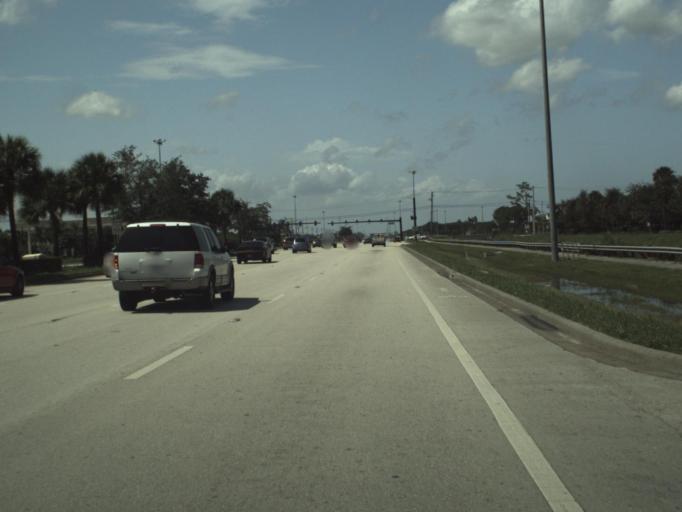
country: US
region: Florida
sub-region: Palm Beach County
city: Wellington
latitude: 26.6256
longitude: -80.2044
